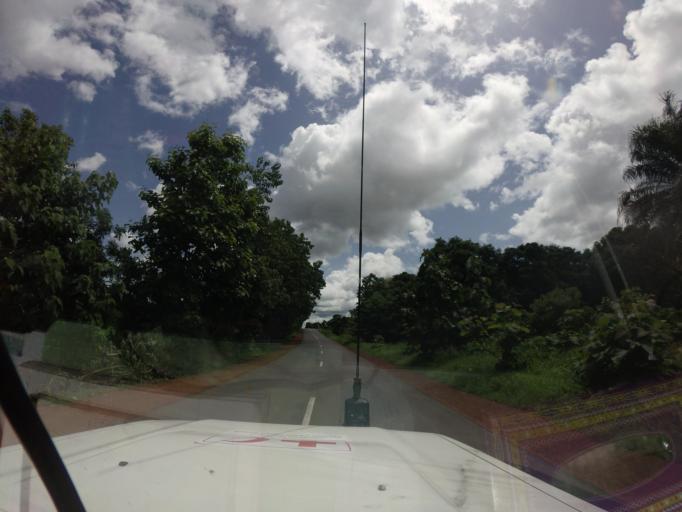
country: SL
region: Northern Province
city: Bindi
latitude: 10.1374
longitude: -11.6485
